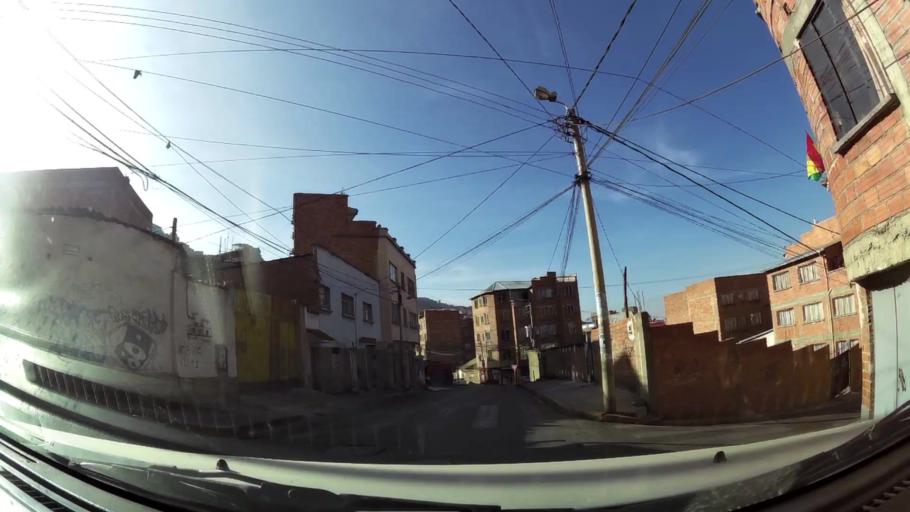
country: BO
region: La Paz
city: La Paz
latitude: -16.4935
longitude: -68.1153
